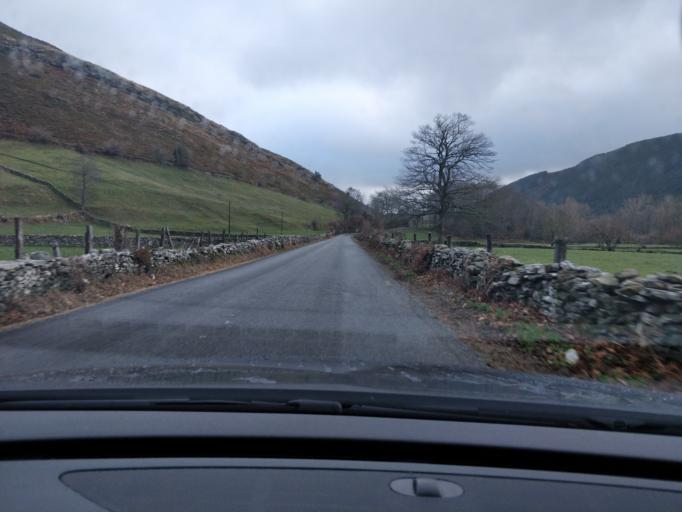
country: ES
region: Castille and Leon
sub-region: Provincia de Burgos
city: Espinosa de los Monteros
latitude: 43.1057
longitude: -3.5734
